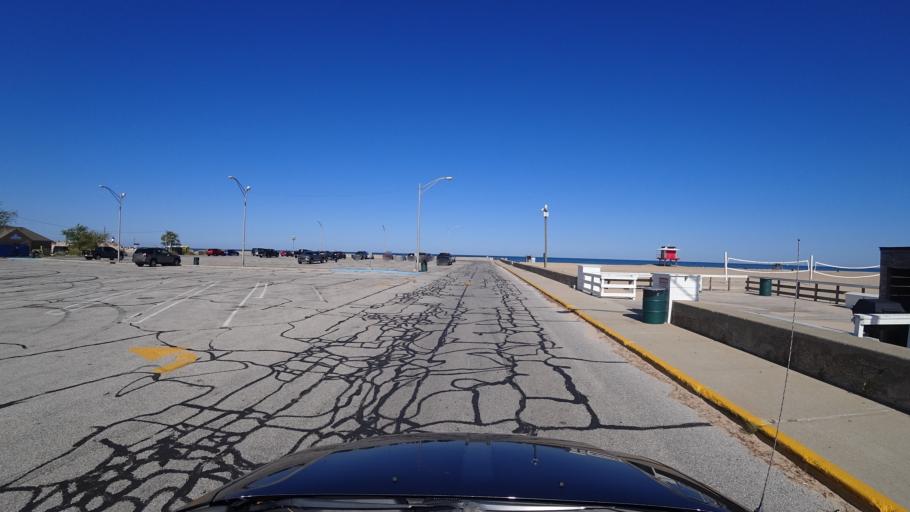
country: US
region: Indiana
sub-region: LaPorte County
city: Michigan City
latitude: 41.7271
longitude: -86.9039
